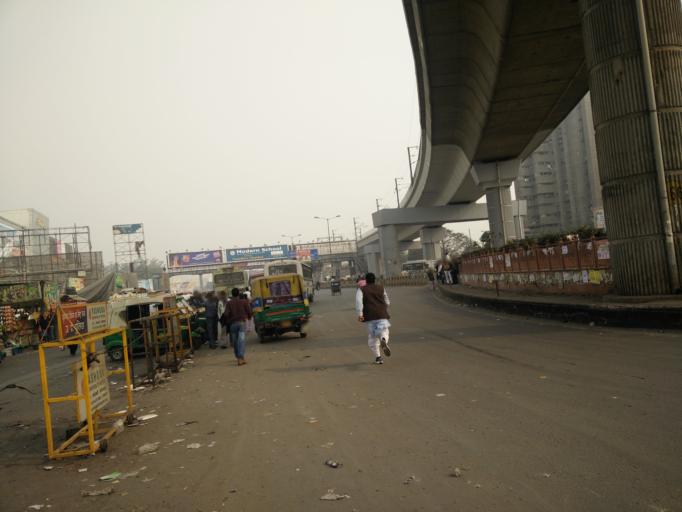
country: IN
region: Uttar Pradesh
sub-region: Gautam Buddha Nagar
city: Noida
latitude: 28.6457
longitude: 77.3183
